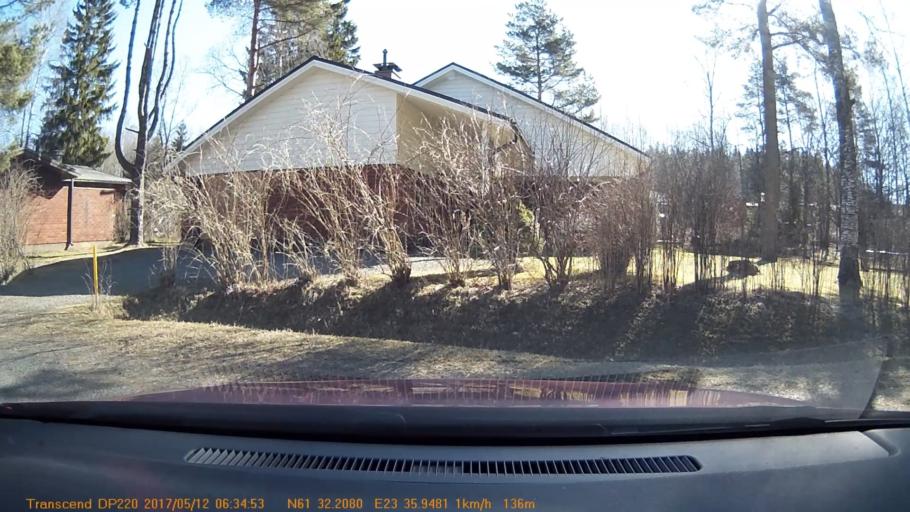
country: FI
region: Pirkanmaa
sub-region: Tampere
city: Yloejaervi
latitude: 61.5368
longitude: 23.5991
